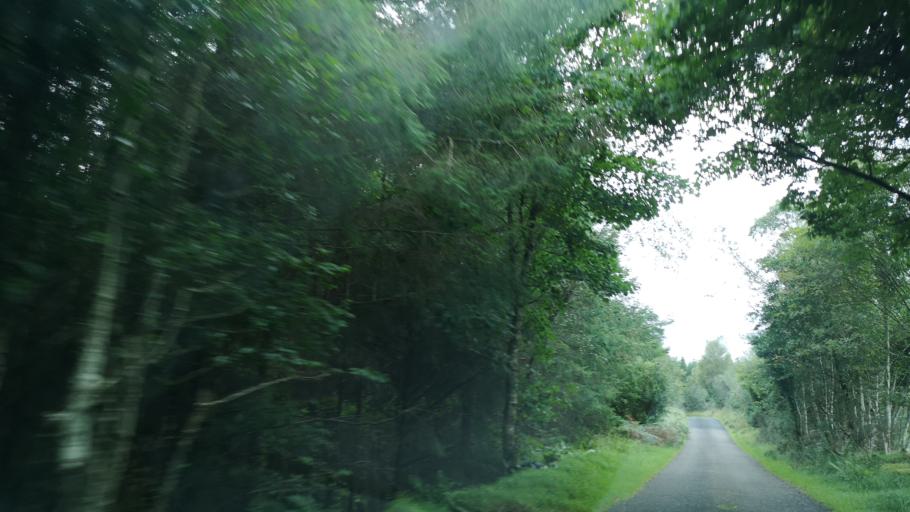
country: IE
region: Connaught
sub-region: County Galway
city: Loughrea
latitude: 53.1352
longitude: -8.4932
